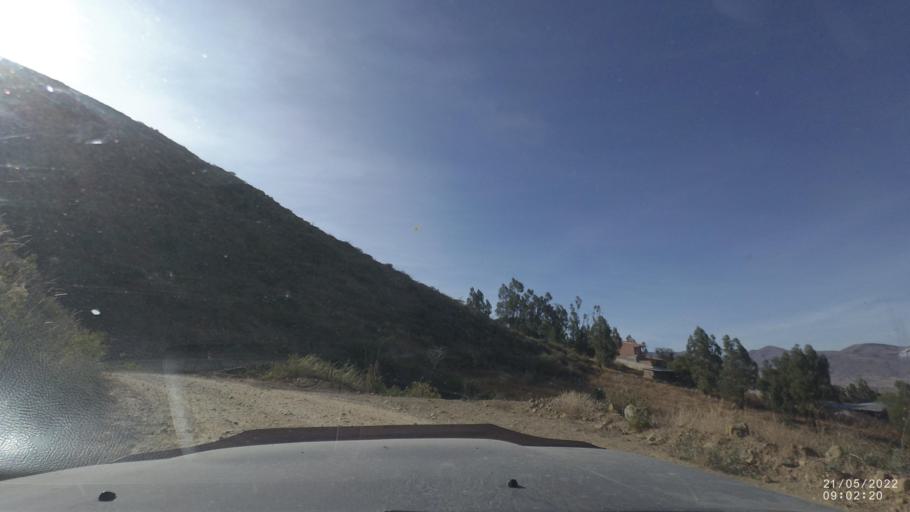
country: BO
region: Cochabamba
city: Cochabamba
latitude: -17.3766
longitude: -66.0314
